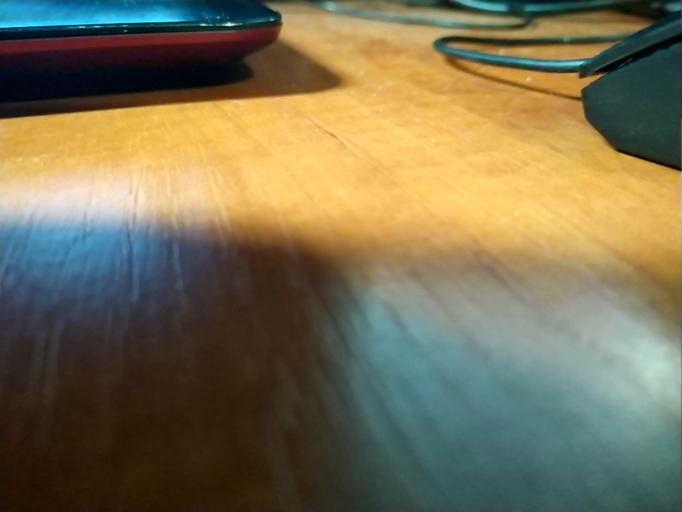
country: RU
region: Tverskaya
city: Likhoslavl'
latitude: 57.2190
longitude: 35.7162
